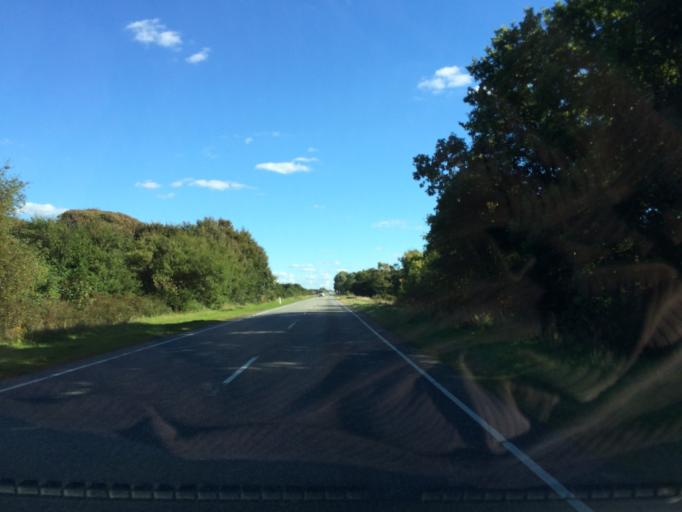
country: DK
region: Central Jutland
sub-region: Holstebro Kommune
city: Holstebro
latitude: 56.3262
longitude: 8.6656
